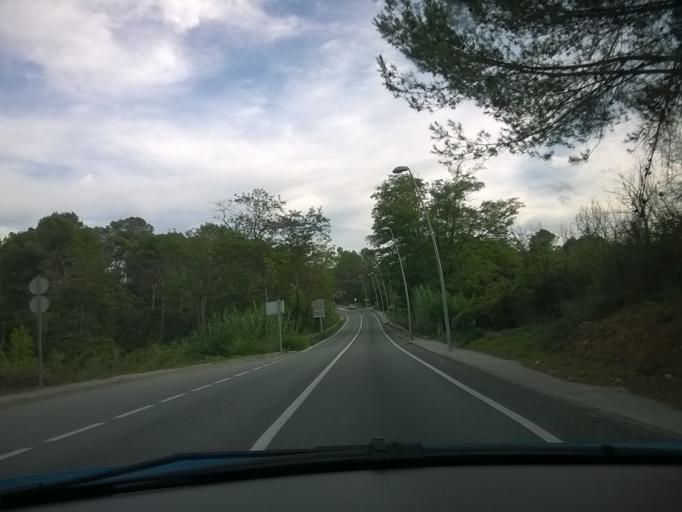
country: ES
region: Catalonia
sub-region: Provincia de Barcelona
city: Sant Cugat del Valles
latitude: 41.4636
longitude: 2.0873
